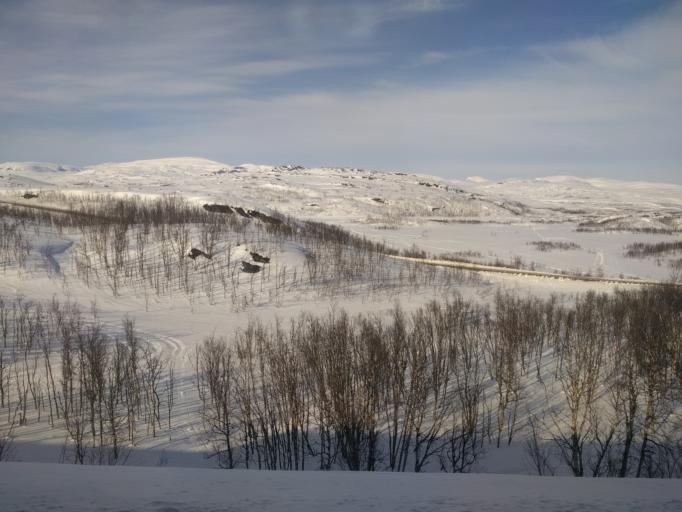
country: NO
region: Troms
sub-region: Bardu
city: Setermoen
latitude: 68.4228
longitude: 18.2856
